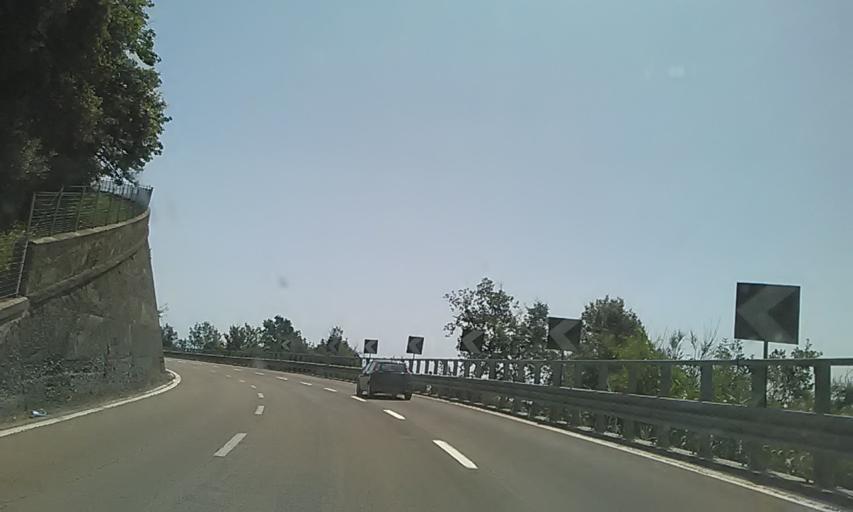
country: IT
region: Liguria
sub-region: Provincia di Genova
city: Arenzano
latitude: 44.4176
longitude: 8.7183
